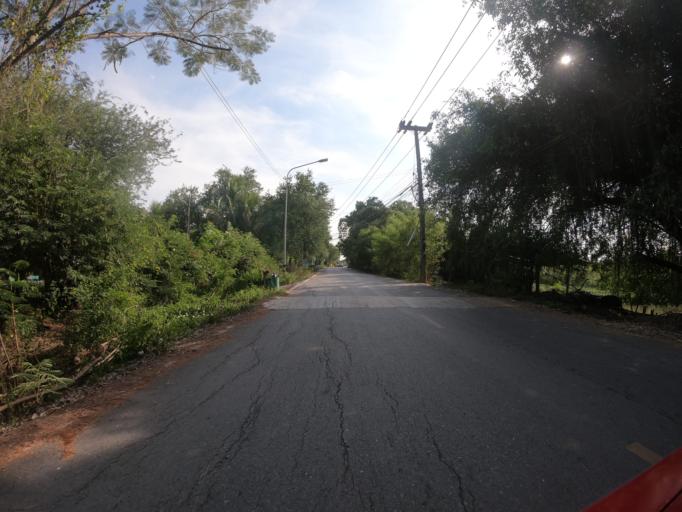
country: TH
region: Pathum Thani
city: Thanyaburi
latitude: 14.0105
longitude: 100.7319
